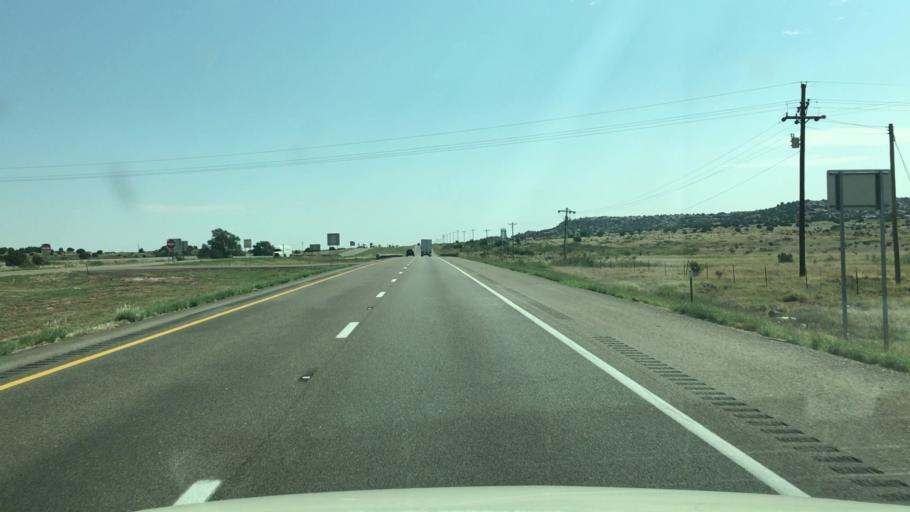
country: US
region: New Mexico
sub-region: Guadalupe County
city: Santa Rosa
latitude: 34.9549
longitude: -104.6242
